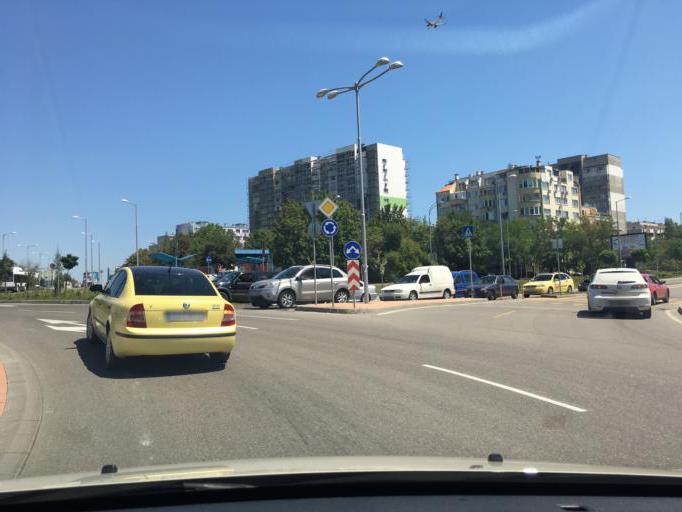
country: BG
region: Burgas
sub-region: Obshtina Burgas
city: Burgas
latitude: 42.5204
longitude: 27.4398
